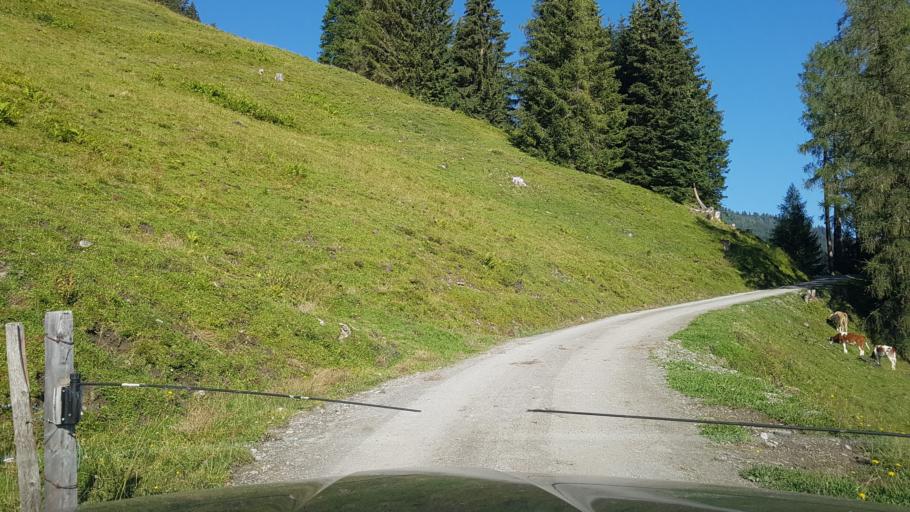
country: AT
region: Salzburg
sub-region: Politischer Bezirk Sankt Johann im Pongau
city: Dorfgastein
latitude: 47.2472
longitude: 13.0743
